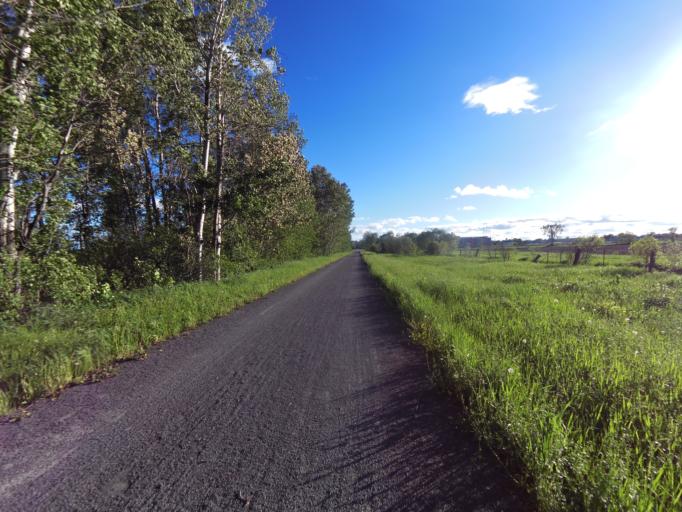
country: CA
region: Ontario
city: Bells Corners
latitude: 45.2761
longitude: -75.8923
